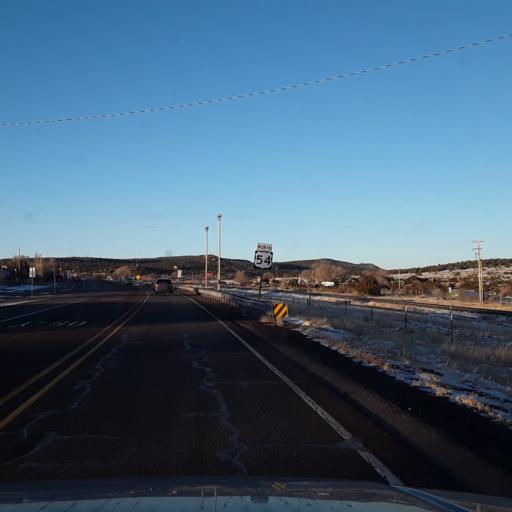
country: US
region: New Mexico
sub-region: Lincoln County
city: Carrizozo
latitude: 34.2449
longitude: -105.5952
